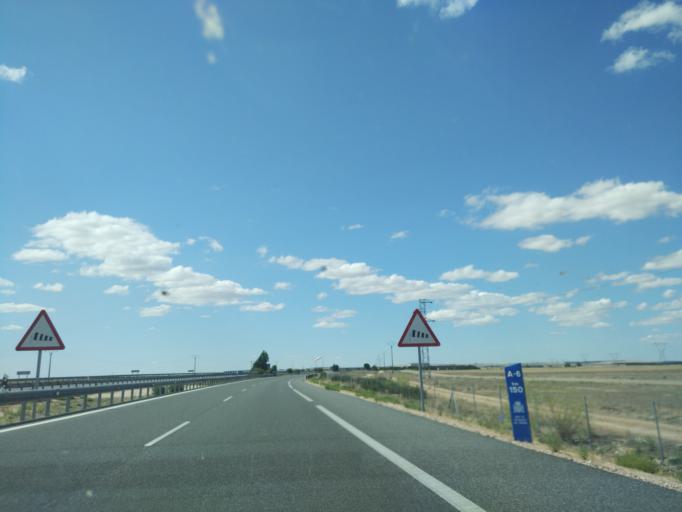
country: ES
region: Castille and Leon
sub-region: Provincia de Valladolid
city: San Vicente del Palacio
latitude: 41.2425
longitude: -4.8646
